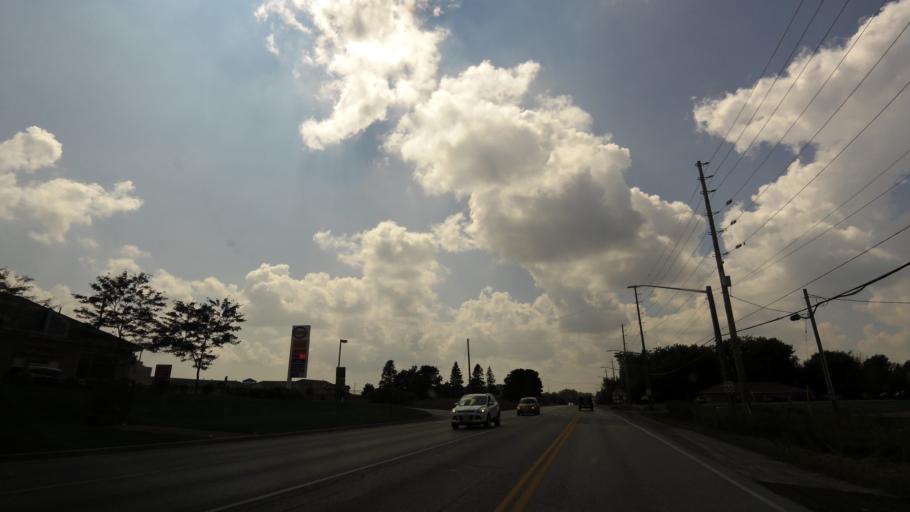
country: CA
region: Ontario
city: Oshawa
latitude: 43.9574
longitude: -78.9438
